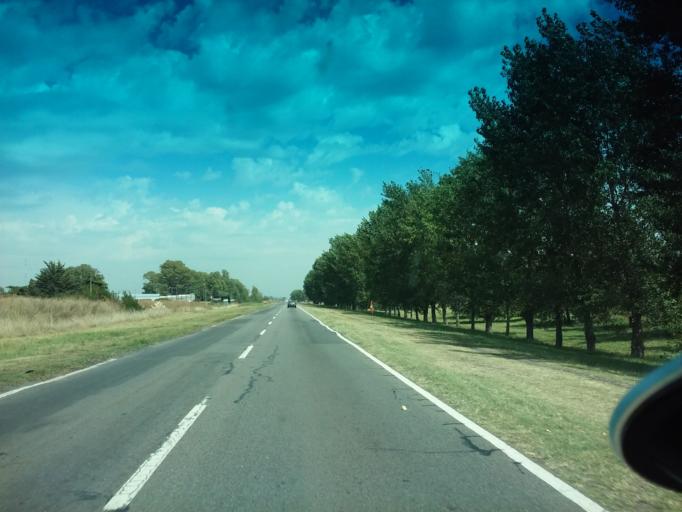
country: AR
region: Buenos Aires
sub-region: Partido de Carlos Casares
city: Carlos Casares
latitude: -35.6290
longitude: -61.3361
